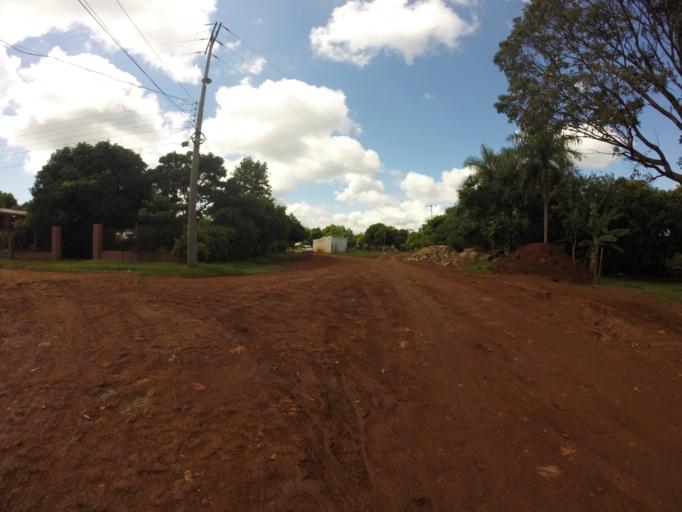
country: PY
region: Alto Parana
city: Ciudad del Este
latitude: -25.3991
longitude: -54.6362
